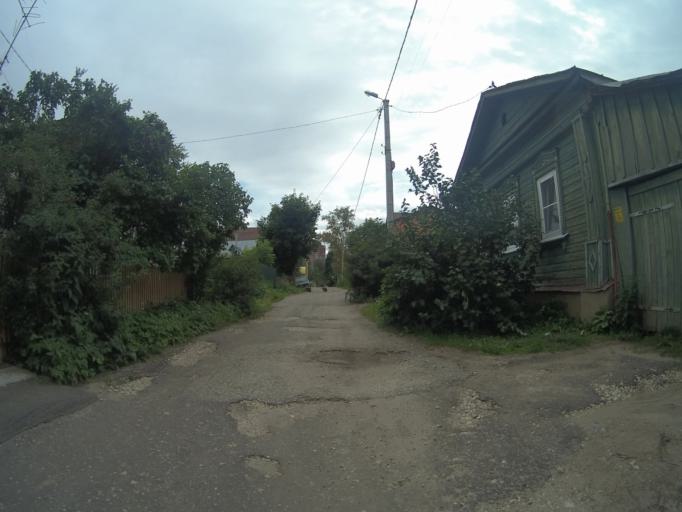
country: RU
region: Vladimir
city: Vladimir
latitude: 56.1281
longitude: 40.3849
